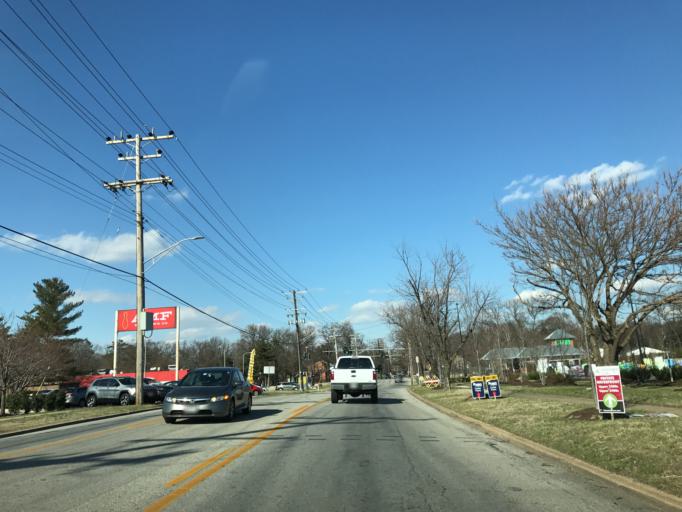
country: US
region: Maryland
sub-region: Anne Arundel County
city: Pasadena
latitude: 39.1269
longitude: -76.5892
